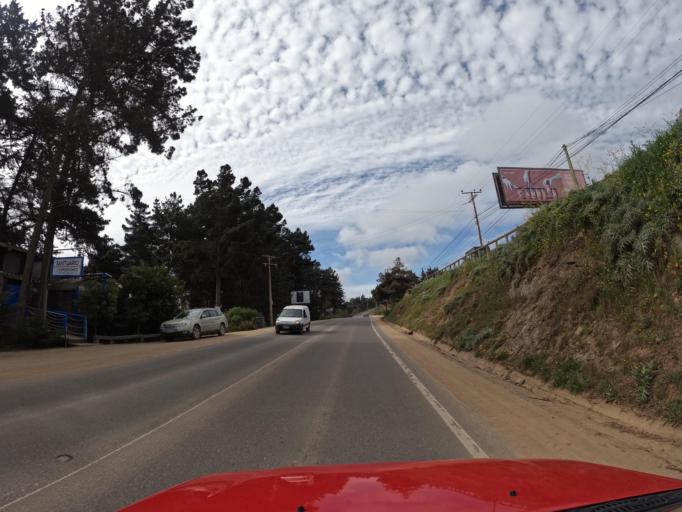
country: CL
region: O'Higgins
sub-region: Provincia de Colchagua
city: Santa Cruz
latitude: -34.4280
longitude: -72.0318
